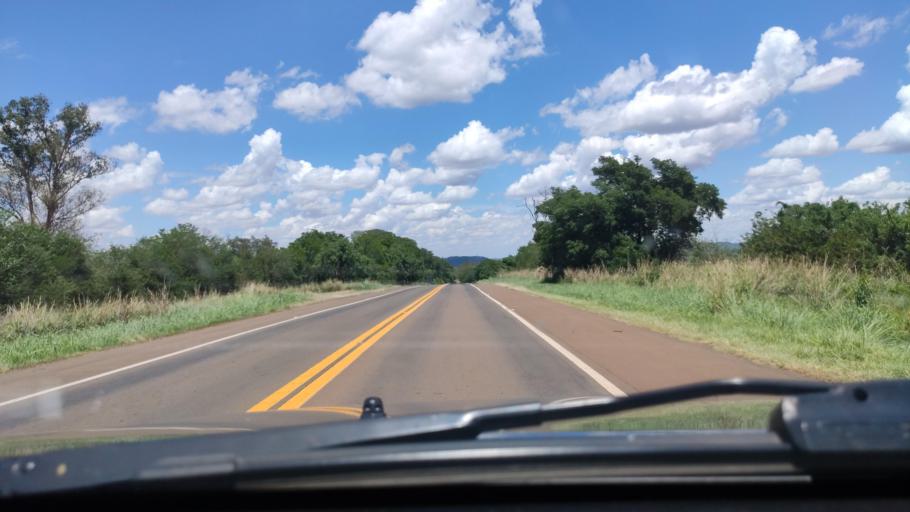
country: BR
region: Sao Paulo
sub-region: Boa Esperanca Do Sul
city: Boa Esperanca do Sul
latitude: -22.0696
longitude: -48.4094
